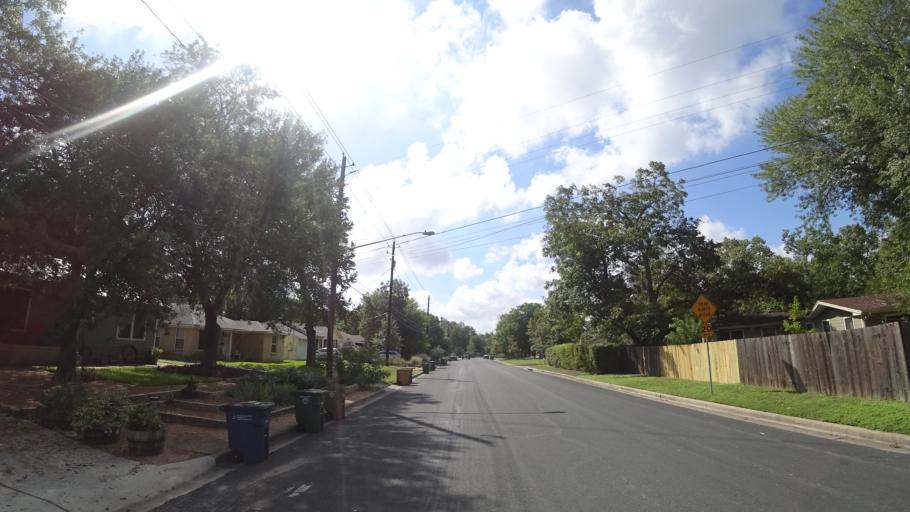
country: US
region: Texas
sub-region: Travis County
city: Austin
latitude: 30.3440
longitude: -97.7219
